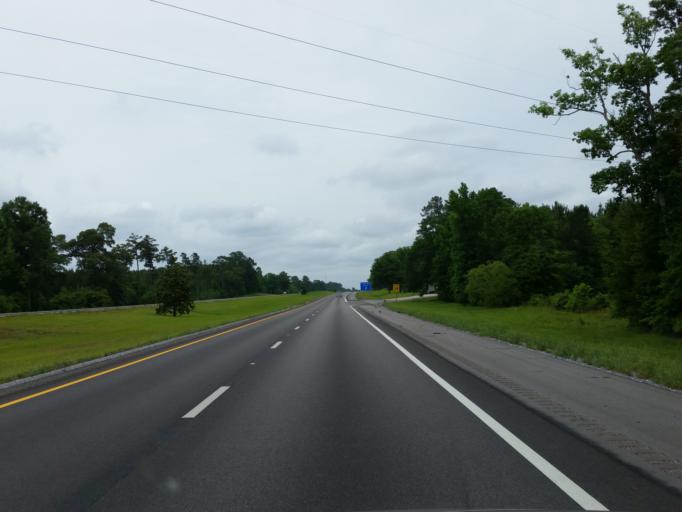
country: US
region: Mississippi
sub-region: Jones County
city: Sharon
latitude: 31.8010
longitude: -89.0538
